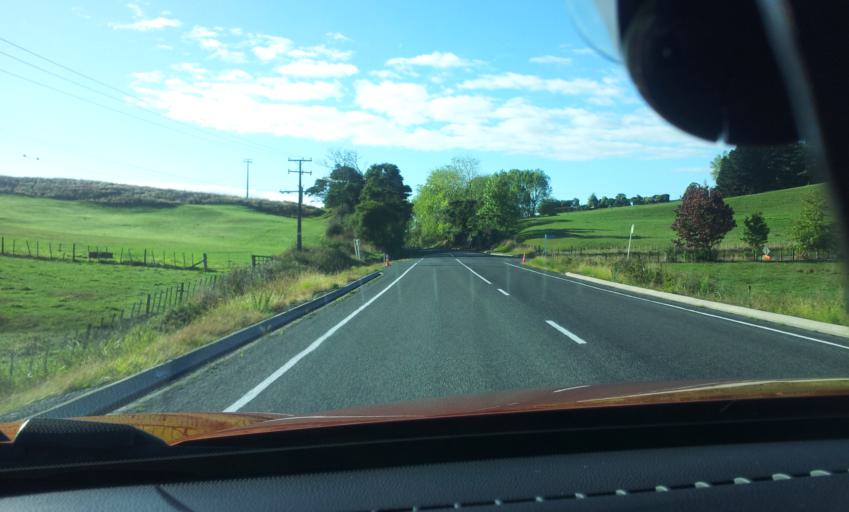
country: NZ
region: Waikato
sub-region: Hauraki District
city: Ngatea
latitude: -37.3122
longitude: 175.3847
